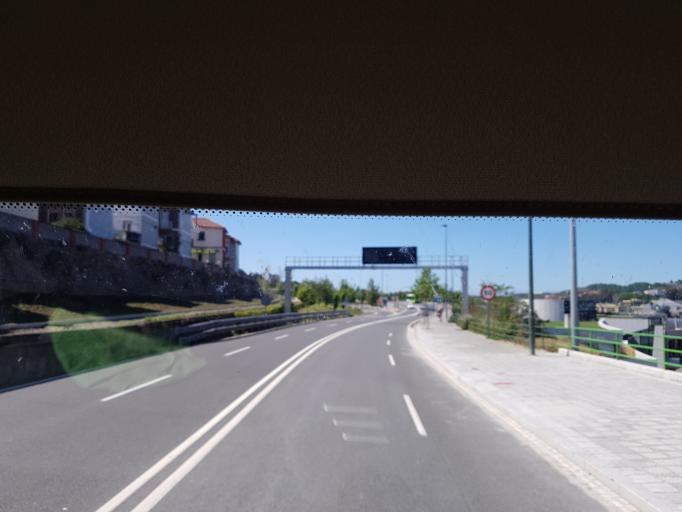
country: ES
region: Basque Country
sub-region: Bizkaia
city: Bilbao
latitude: 43.2611
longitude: -2.9554
